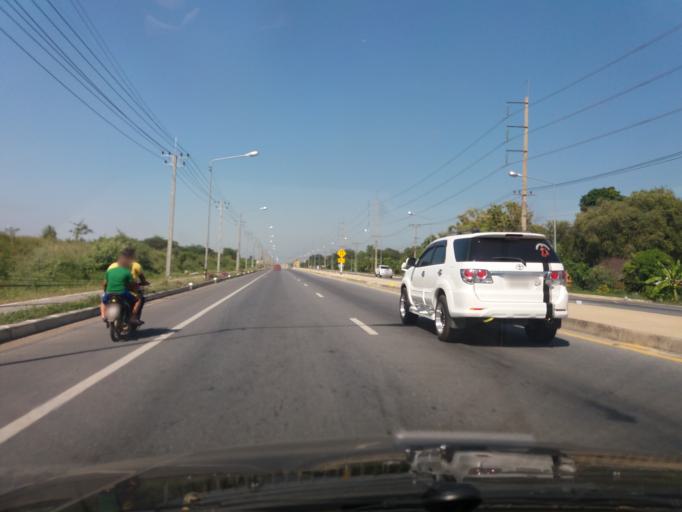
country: TH
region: Chai Nat
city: Manorom
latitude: 15.2671
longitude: 100.0930
